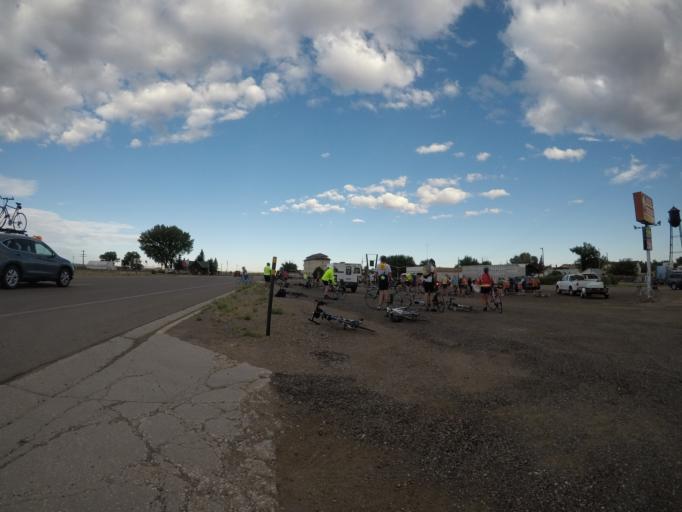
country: US
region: Wyoming
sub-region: Carbon County
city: Saratoga
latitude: 41.8957
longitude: -106.1983
